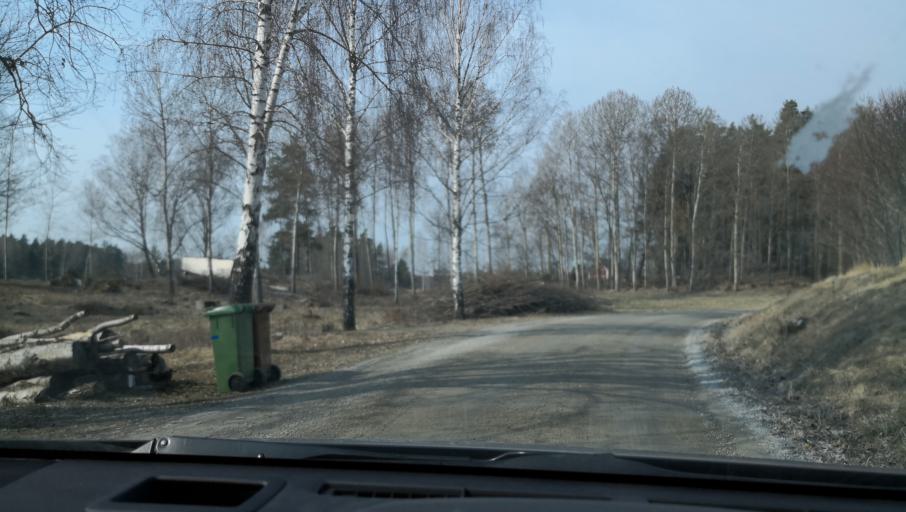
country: SE
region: OErebro
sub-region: Lindesbergs Kommun
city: Frovi
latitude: 59.3479
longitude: 15.4390
